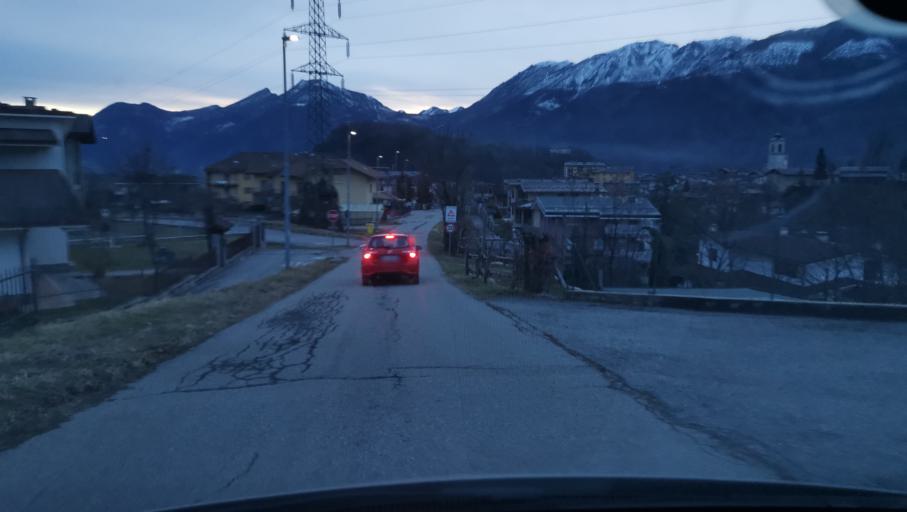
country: IT
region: Piedmont
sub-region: Provincia di Cuneo
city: Demonte
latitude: 44.3189
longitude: 7.2948
